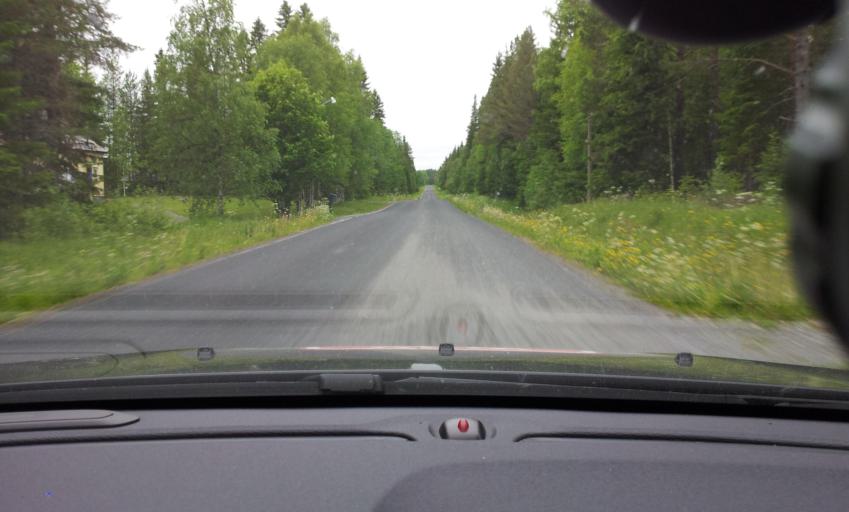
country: SE
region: Jaemtland
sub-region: Krokoms Kommun
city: Valla
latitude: 63.2775
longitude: 13.9042
